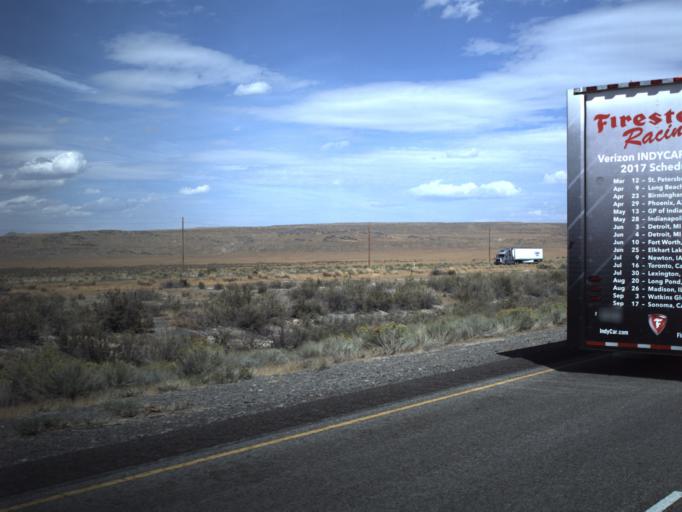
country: US
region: Utah
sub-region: Tooele County
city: Grantsville
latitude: 40.7479
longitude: -113.0539
